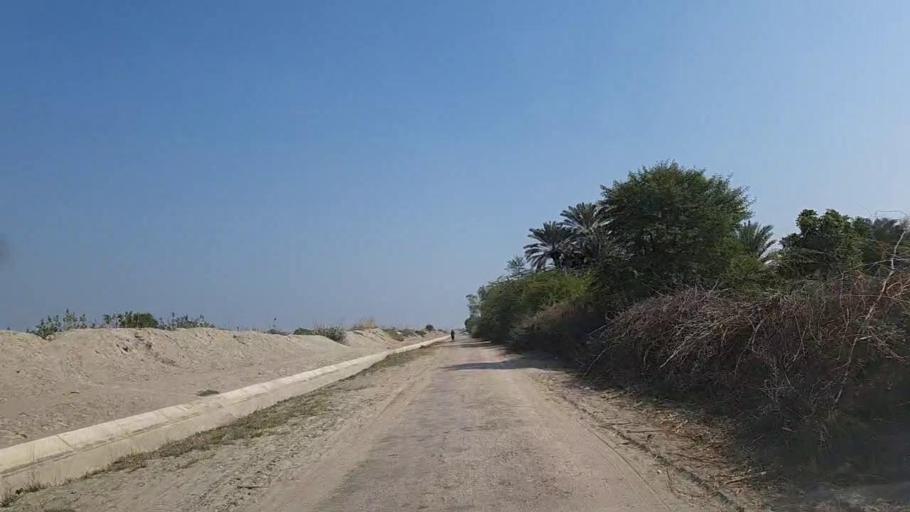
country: PK
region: Sindh
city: Jam Sahib
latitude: 26.2716
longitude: 68.5610
